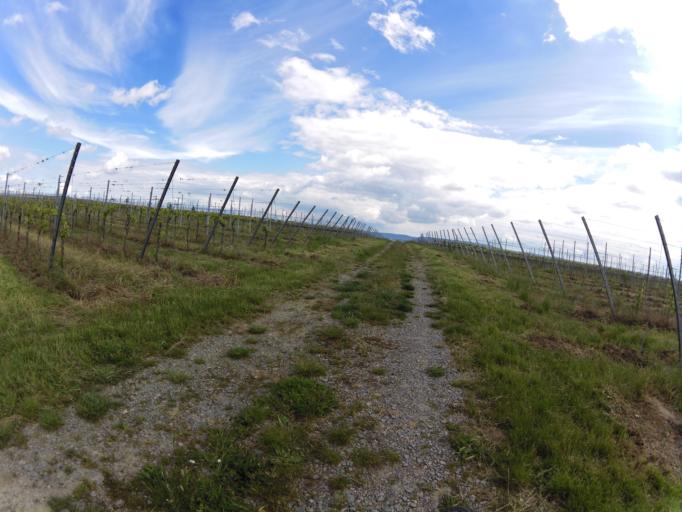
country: DE
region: Bavaria
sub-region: Regierungsbezirk Unterfranken
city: Sommerach
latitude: 49.8410
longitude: 10.1937
